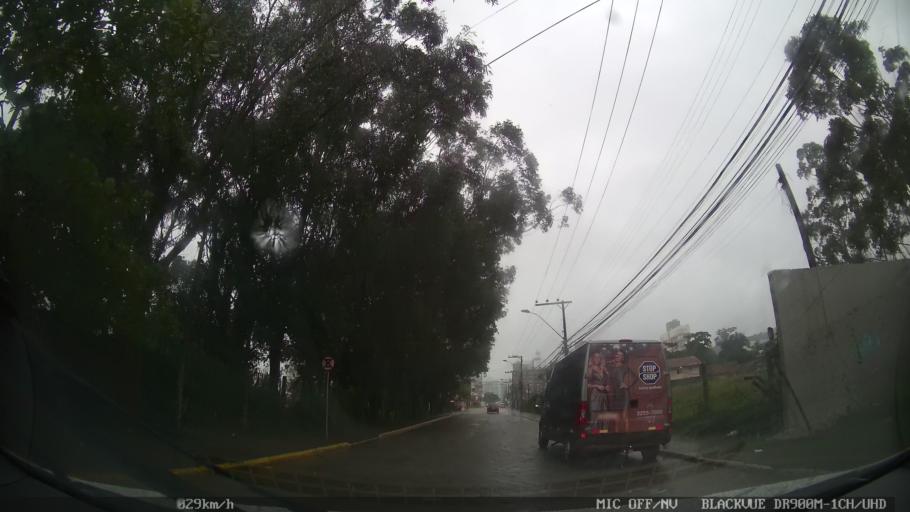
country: BR
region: Santa Catarina
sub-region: Balneario Camboriu
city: Balneario Camboriu
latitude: -26.9468
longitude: -48.6305
